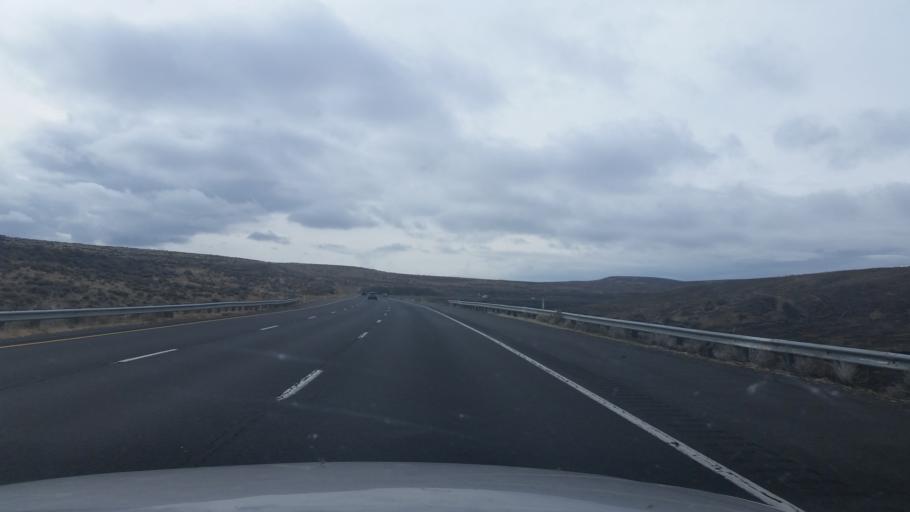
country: US
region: Washington
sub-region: Grant County
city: Mattawa
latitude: 46.9413
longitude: -120.1206
